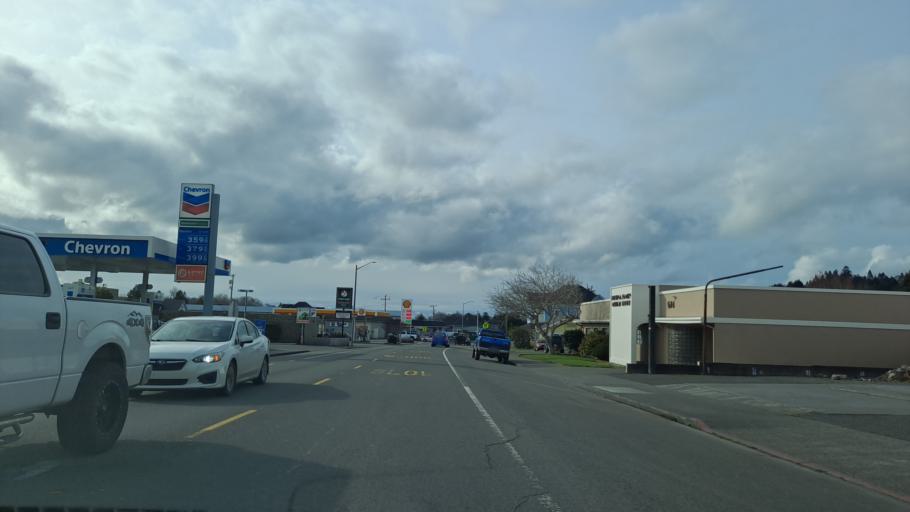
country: US
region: California
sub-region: Humboldt County
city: Fortuna
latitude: 40.5980
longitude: -124.1577
